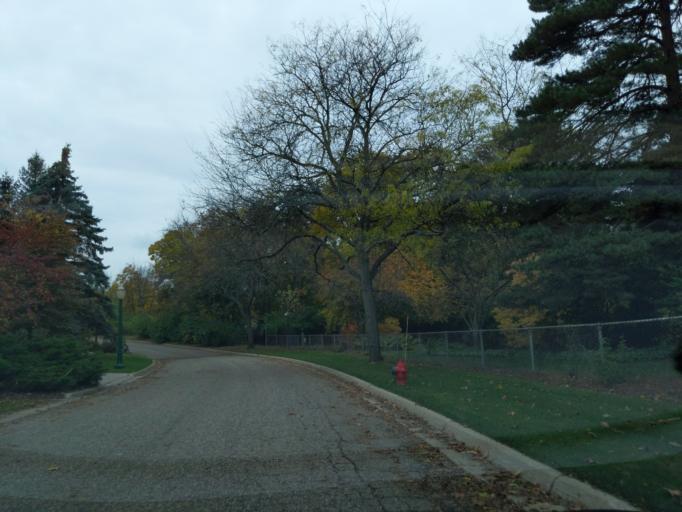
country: US
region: Michigan
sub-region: Ingham County
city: Edgemont Park
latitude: 42.7189
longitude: -84.5859
